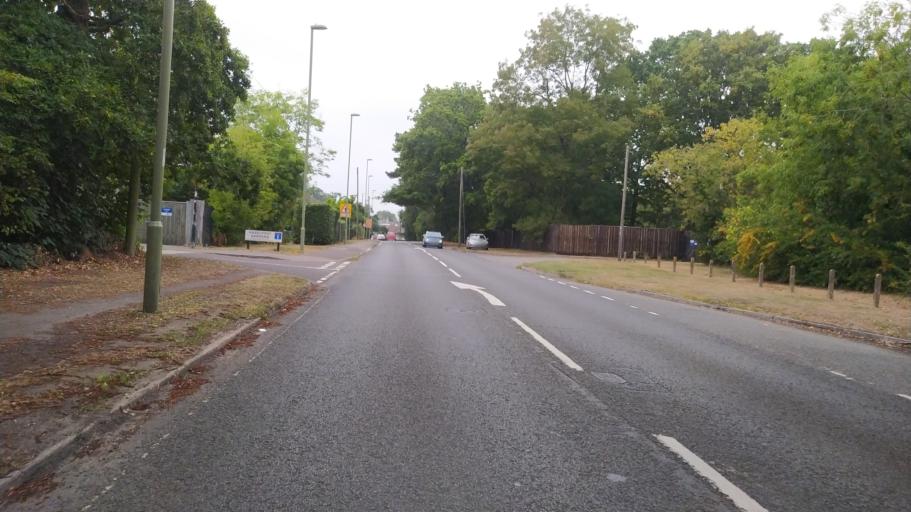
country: GB
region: England
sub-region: Hampshire
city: West End
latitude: 50.9185
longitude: -1.3315
